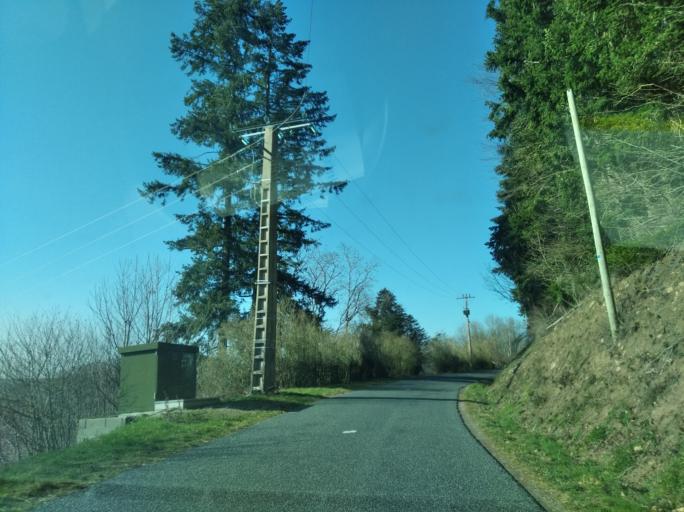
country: FR
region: Auvergne
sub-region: Departement de l'Allier
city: Le Mayet-de-Montagne
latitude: 46.1036
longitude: 3.6807
